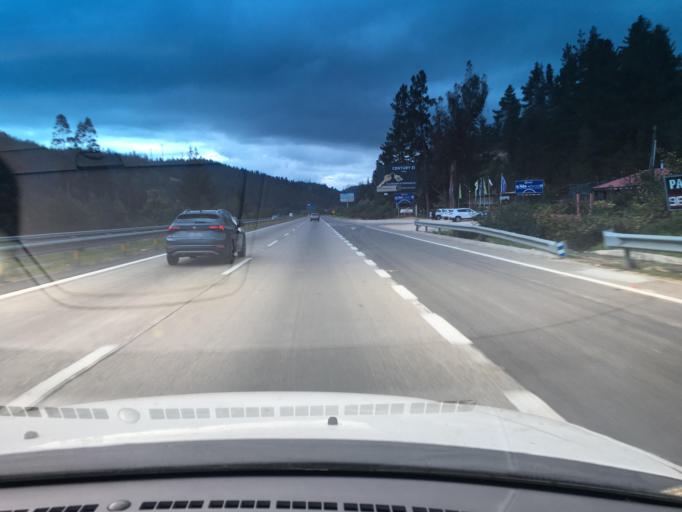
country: CL
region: Valparaiso
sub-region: Provincia de Marga Marga
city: Quilpue
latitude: -33.2317
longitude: -71.4641
